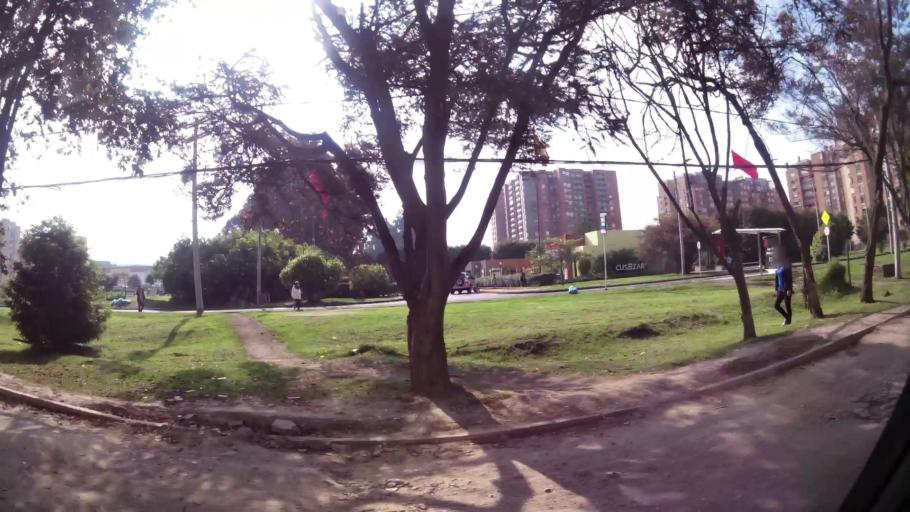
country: CO
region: Bogota D.C.
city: Barrio San Luis
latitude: 4.7349
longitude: -74.0624
